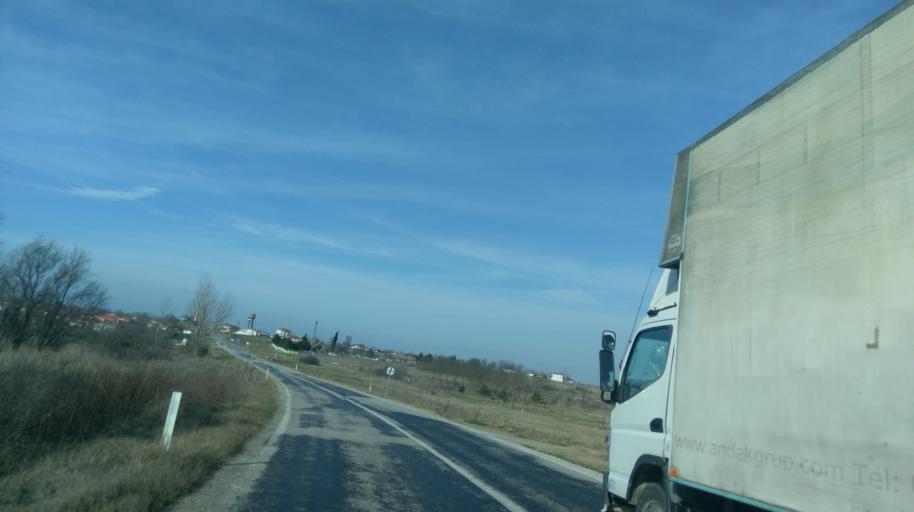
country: TR
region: Edirne
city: Copkoy
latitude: 41.3081
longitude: 26.8354
